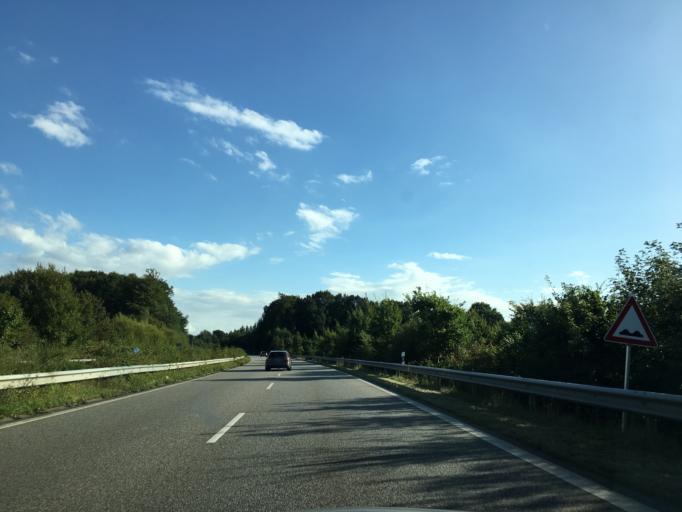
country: DE
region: Schleswig-Holstein
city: Heikendorf
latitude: 54.3556
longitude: 10.2058
